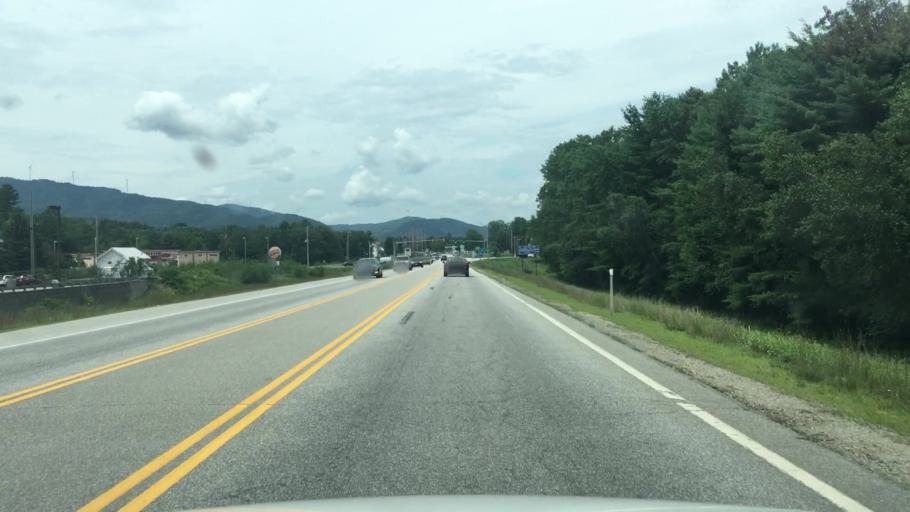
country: US
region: New Hampshire
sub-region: Grafton County
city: Plymouth
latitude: 43.7704
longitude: -71.7182
